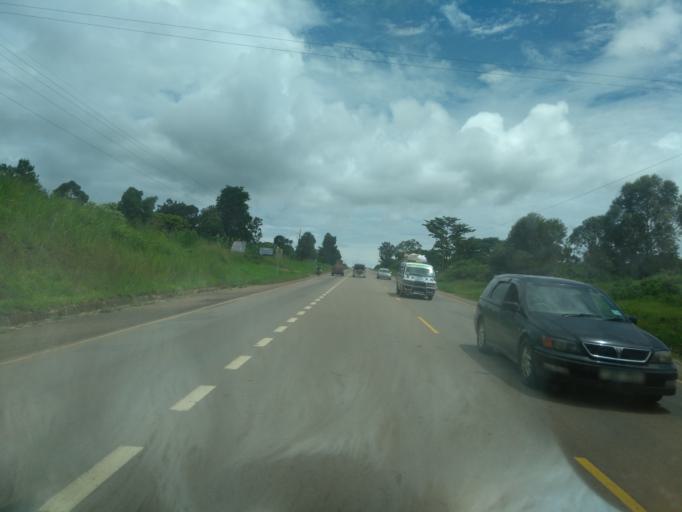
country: UG
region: Central Region
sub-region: Butambala District
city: Gombe
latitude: 0.0075
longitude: 32.0469
